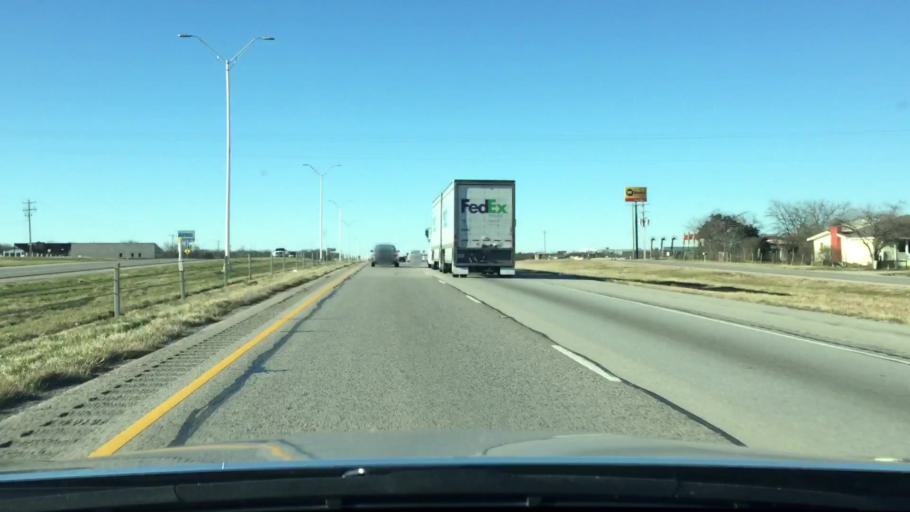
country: US
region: Texas
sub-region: Johnson County
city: Alvarado
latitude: 32.4594
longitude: -97.2627
